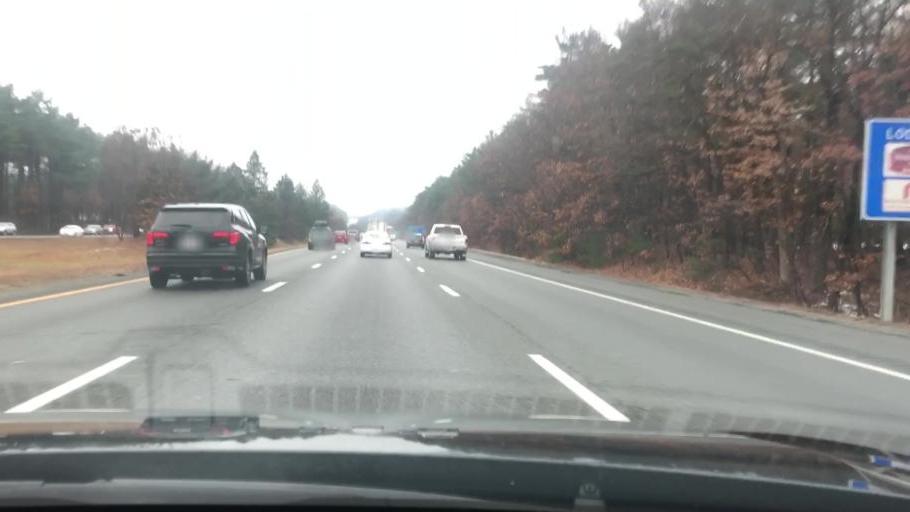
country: US
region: Massachusetts
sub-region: Middlesex County
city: Chelmsford
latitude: 42.5839
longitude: -71.3943
